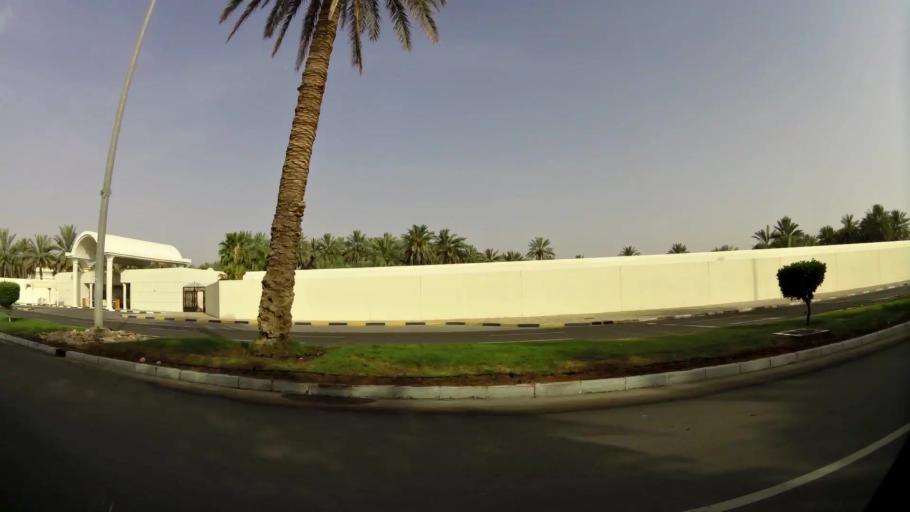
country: AE
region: Abu Dhabi
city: Al Ain
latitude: 24.1299
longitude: 55.6816
